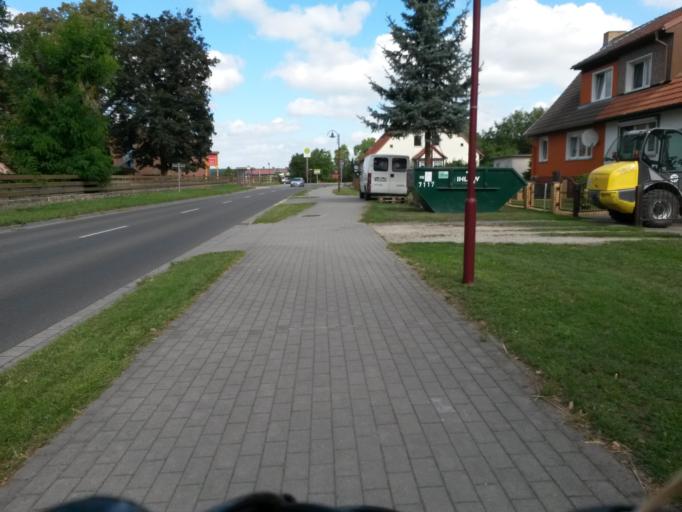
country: DE
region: Brandenburg
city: Angermunde
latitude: 53.0364
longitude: 13.9890
